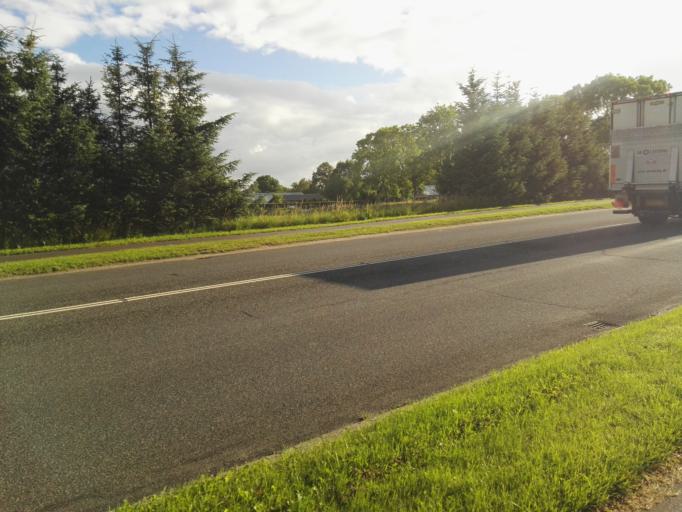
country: DK
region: Capital Region
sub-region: Egedal Kommune
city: Smorumnedre
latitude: 55.7298
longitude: 12.3147
